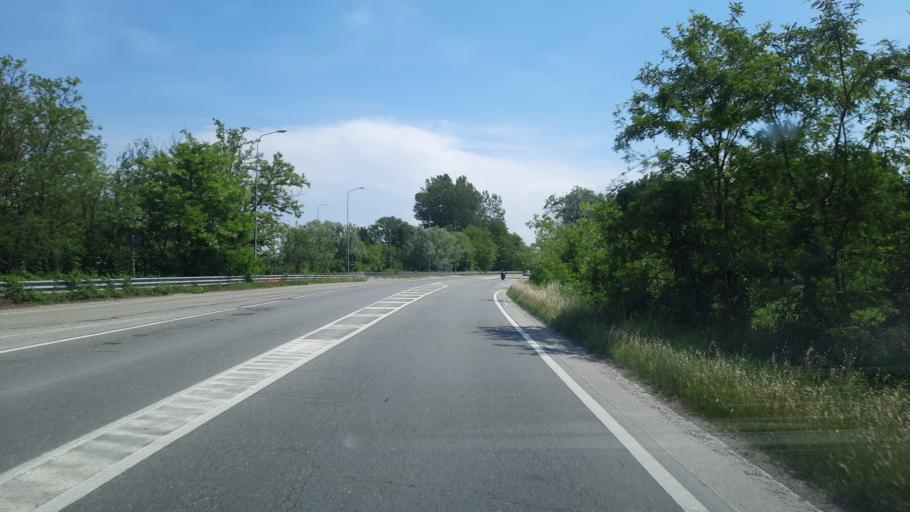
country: IT
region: Lombardy
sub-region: Provincia di Pavia
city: Tromello
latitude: 45.2151
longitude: 8.8573
